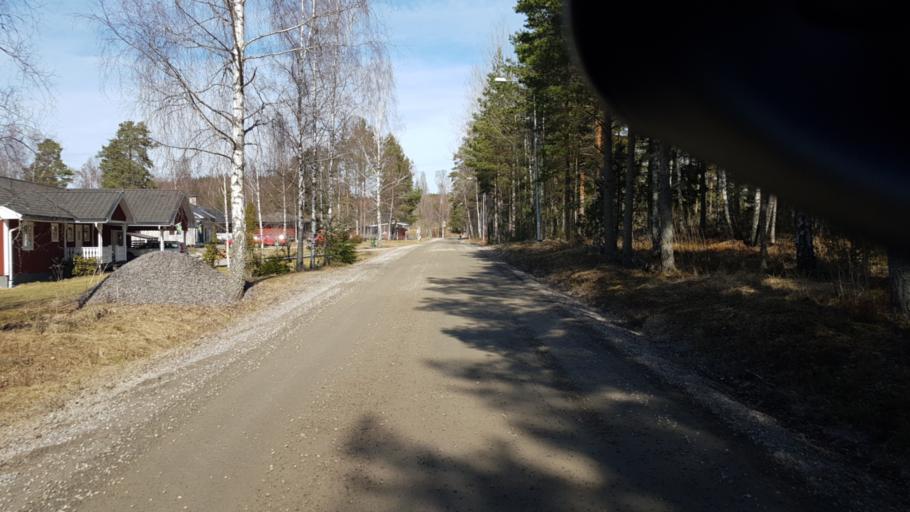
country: SE
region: Vaermland
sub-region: Arvika Kommun
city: Arvika
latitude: 59.5244
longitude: 12.8277
